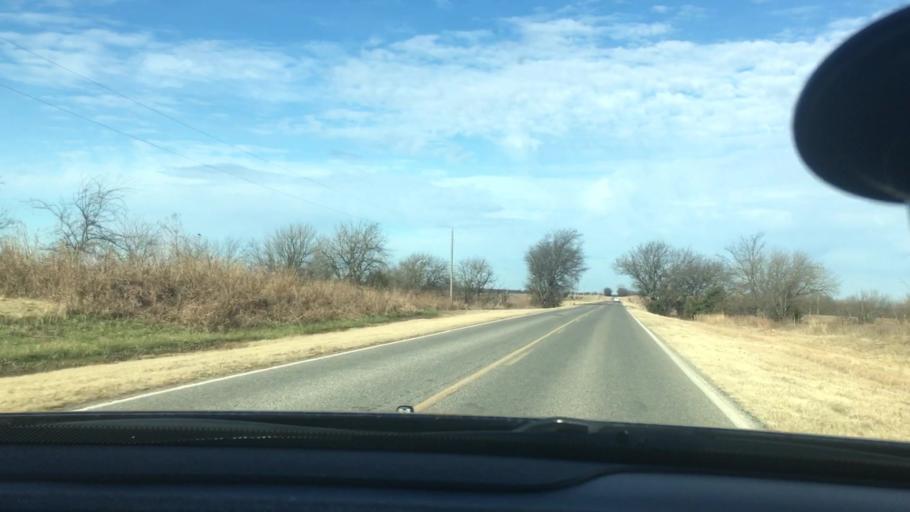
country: US
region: Oklahoma
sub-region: Seminole County
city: Konawa
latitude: 34.9719
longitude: -96.7792
